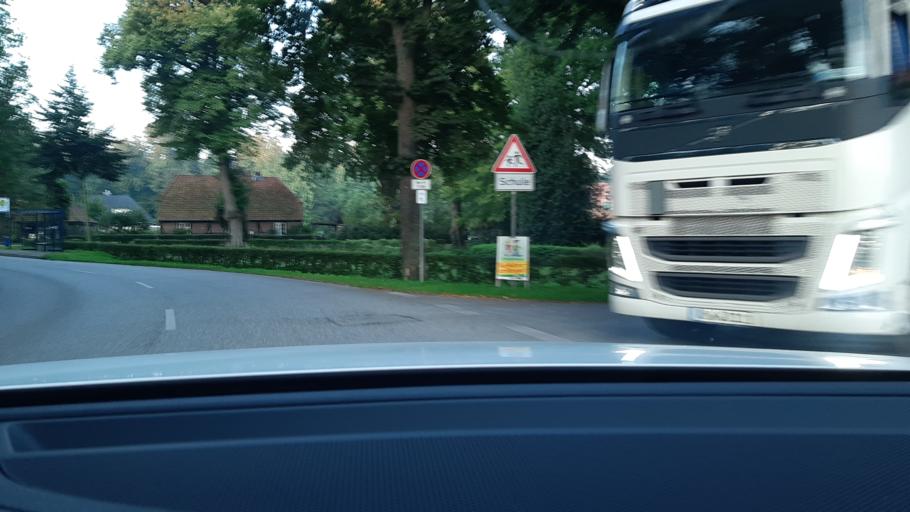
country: DE
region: Schleswig-Holstein
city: Hamberge
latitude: 53.8330
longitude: 10.6100
